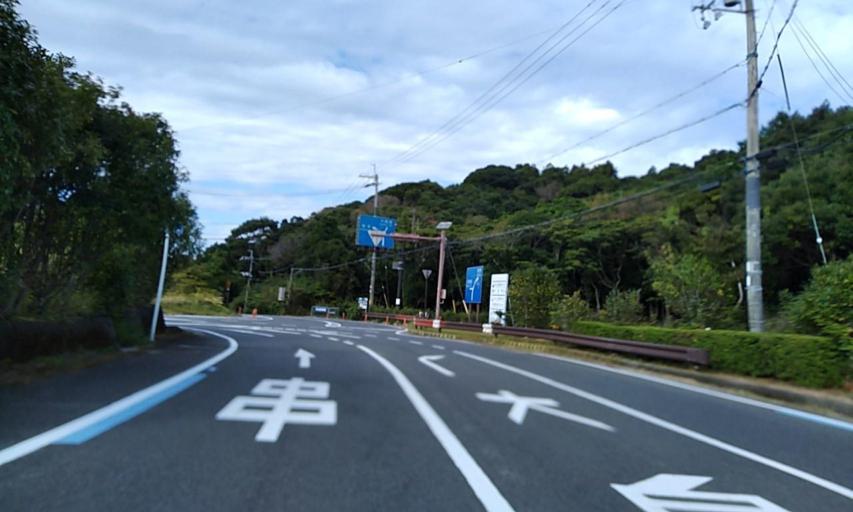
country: JP
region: Wakayama
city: Shingu
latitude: 33.4721
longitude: 135.8174
